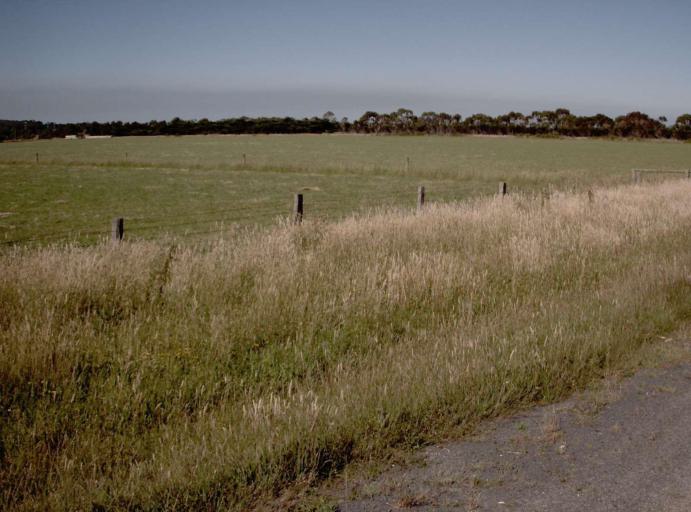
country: AU
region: Victoria
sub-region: Latrobe
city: Morwell
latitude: -38.6321
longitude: 146.5617
